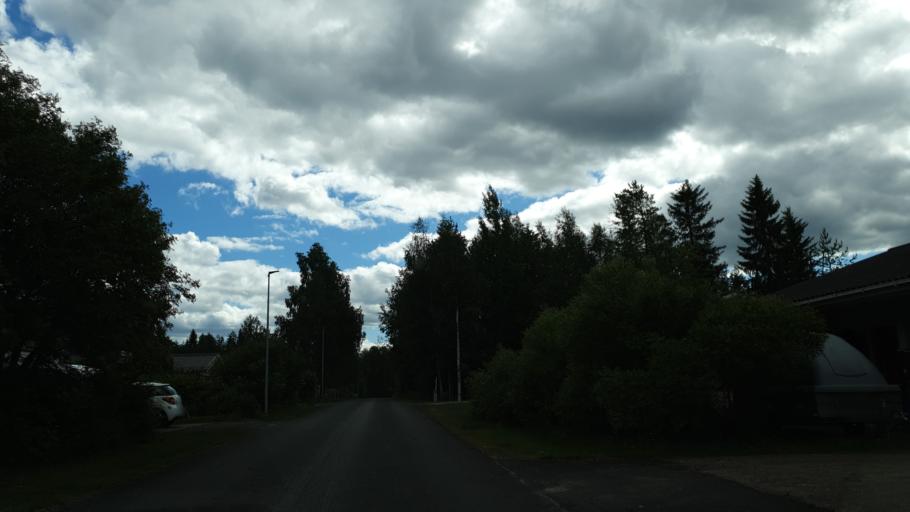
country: FI
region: Kainuu
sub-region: Kehys-Kainuu
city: Kuhmo
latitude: 64.1174
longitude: 29.5020
